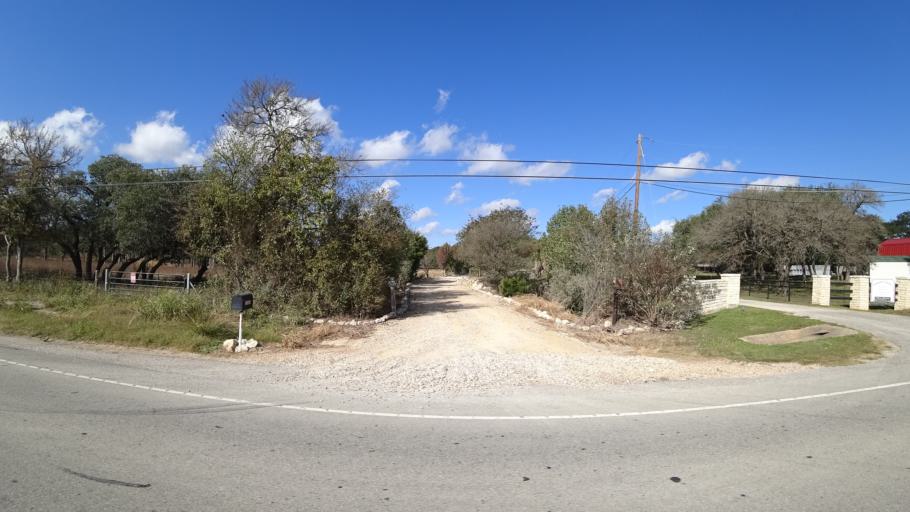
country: US
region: Texas
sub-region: Travis County
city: Shady Hollow
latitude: 30.1959
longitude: -97.9226
